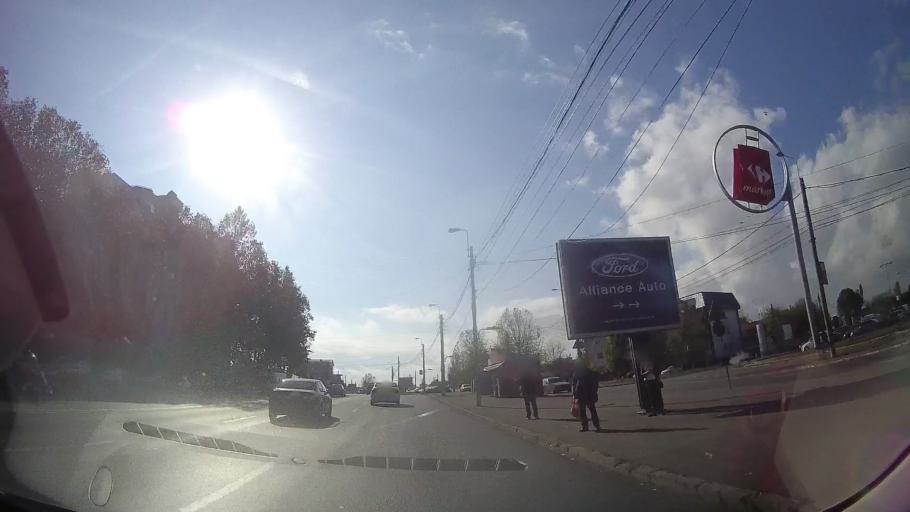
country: RO
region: Constanta
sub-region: Municipiul Constanta
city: Constanta
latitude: 44.1541
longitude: 28.6287
